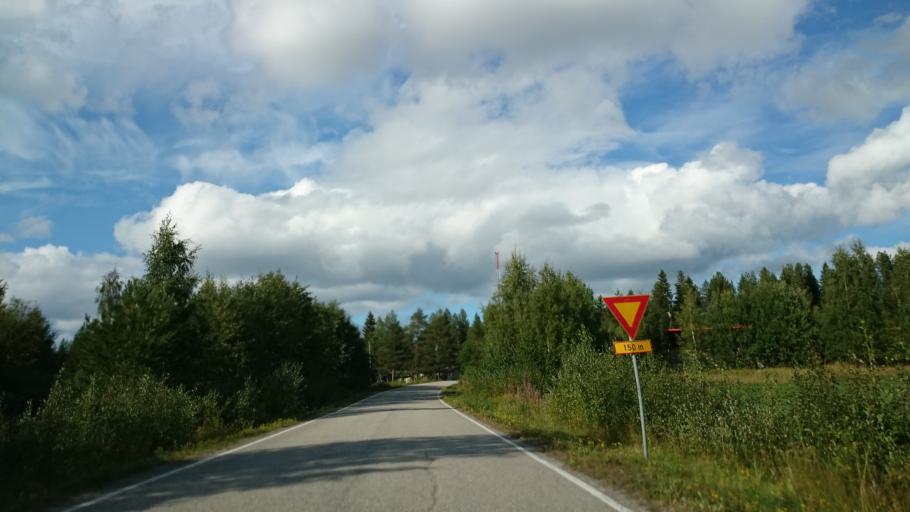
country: FI
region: Kainuu
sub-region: Kehys-Kainuu
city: Suomussalmi
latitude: 64.7458
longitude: 29.4399
